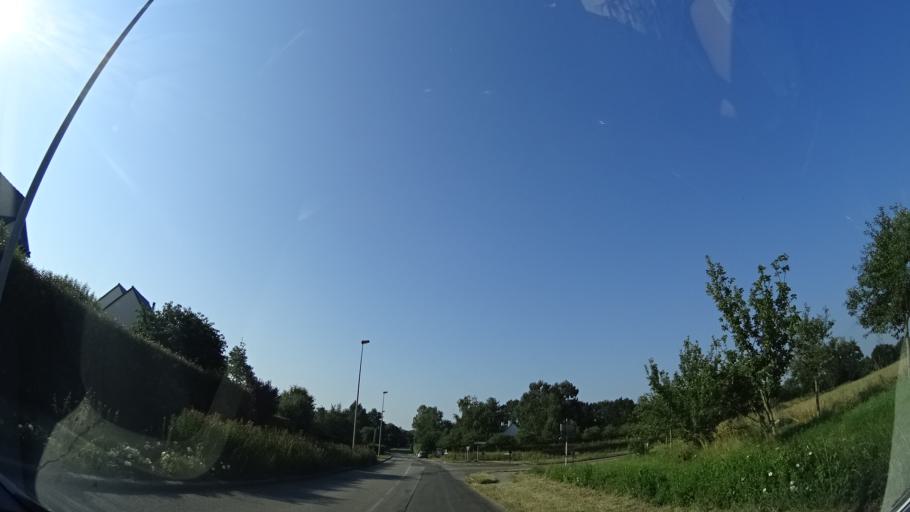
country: FR
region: Brittany
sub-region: Departement d'Ille-et-Vilaine
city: Pace
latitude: 48.1526
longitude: -1.7926
